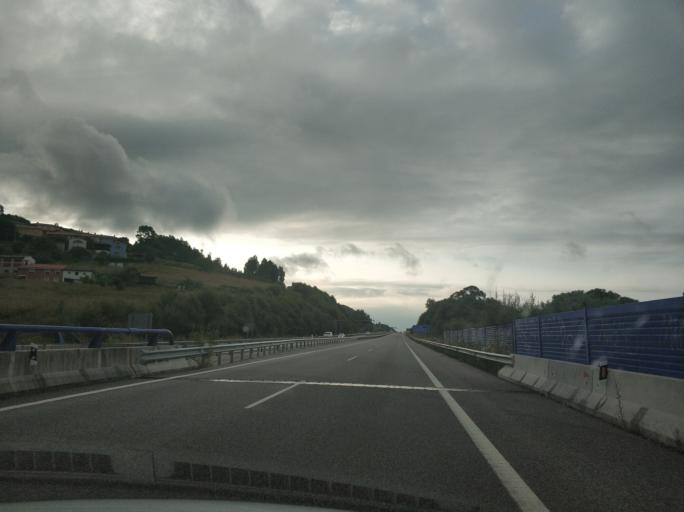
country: ES
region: Asturias
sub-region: Province of Asturias
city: Cudillero
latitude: 43.5461
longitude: -6.1593
